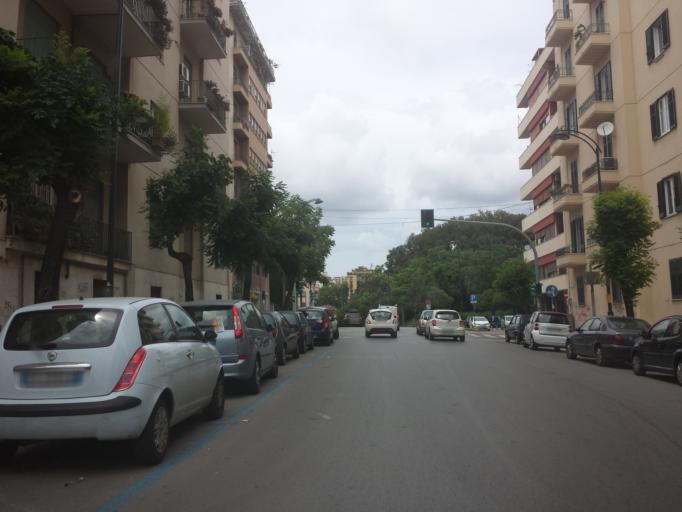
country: IT
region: Sicily
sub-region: Palermo
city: Palermo
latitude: 38.1291
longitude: 13.3496
